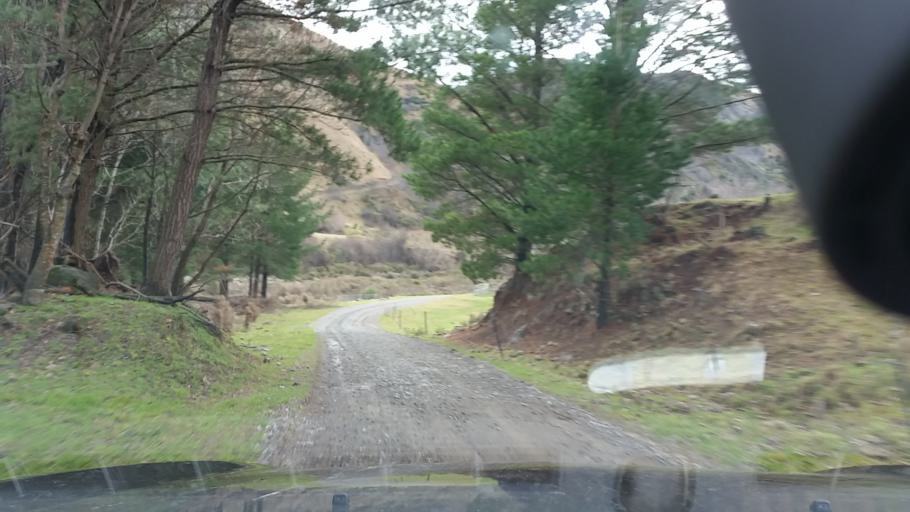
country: NZ
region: Tasman
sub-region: Tasman District
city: Brightwater
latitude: -41.7382
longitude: 173.4190
